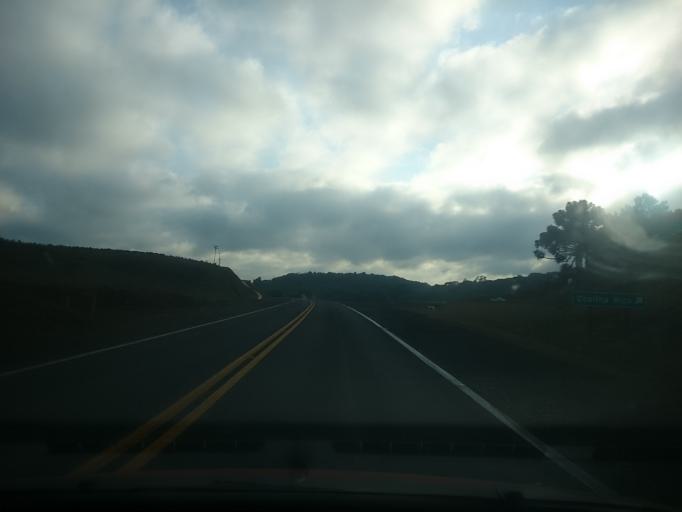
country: BR
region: Rio Grande do Sul
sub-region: Vacaria
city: Estrela
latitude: -28.0771
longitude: -50.5818
